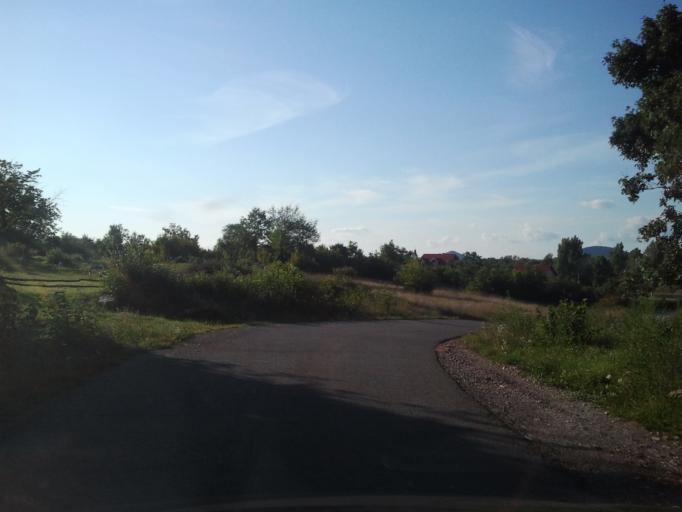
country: HR
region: Zadarska
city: Gracac
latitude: 44.3857
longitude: 15.6935
